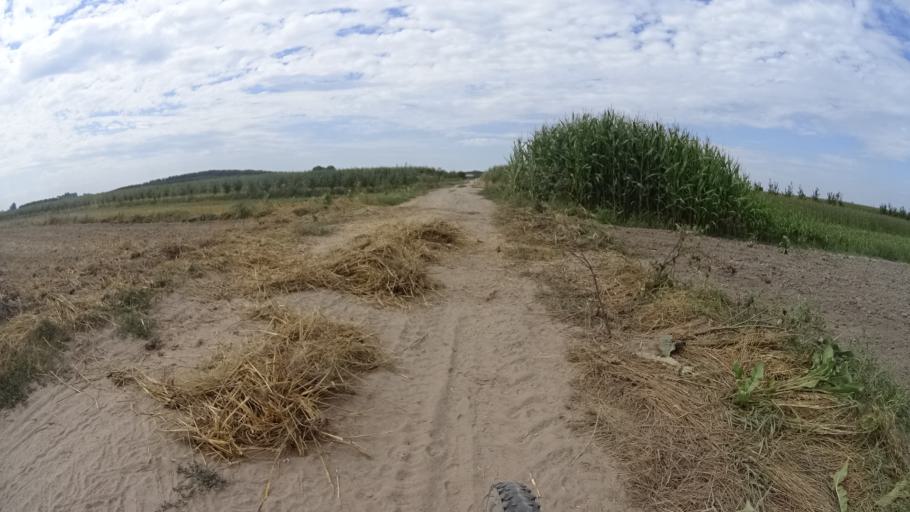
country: PL
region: Masovian Voivodeship
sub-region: Powiat bialobrzeski
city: Wysmierzyce
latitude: 51.6592
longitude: 20.7970
